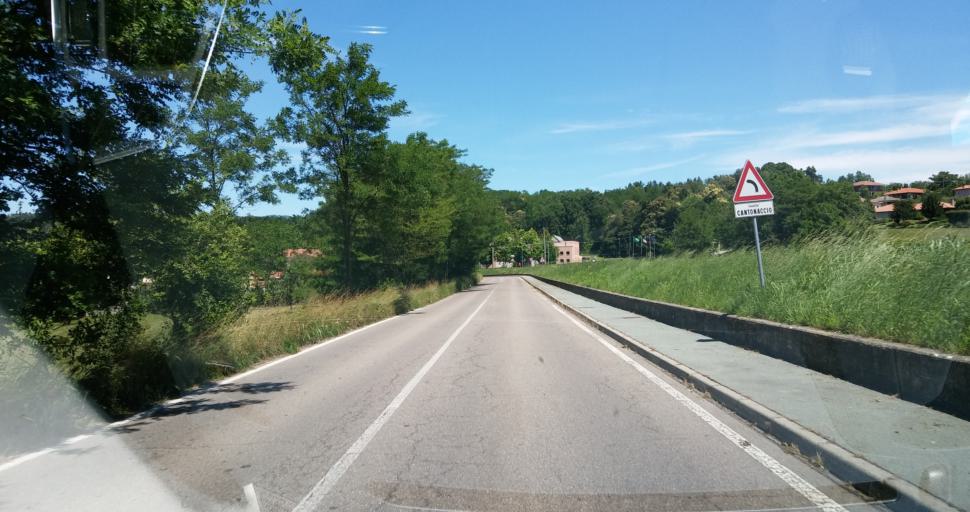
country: IT
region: Lombardy
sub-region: Provincia di Varese
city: Casale Litta
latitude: 45.7556
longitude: 8.7310
